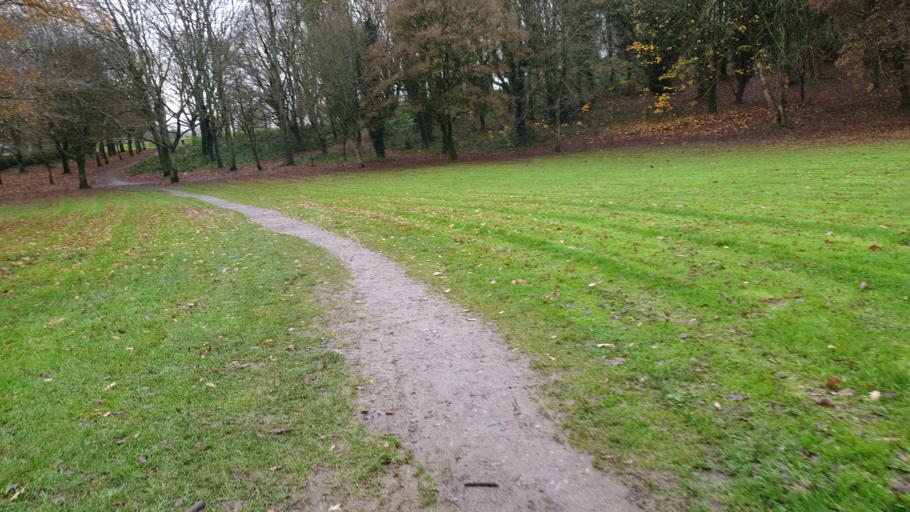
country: IE
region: Munster
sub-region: County Cork
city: Cork
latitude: 51.8924
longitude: -8.4294
